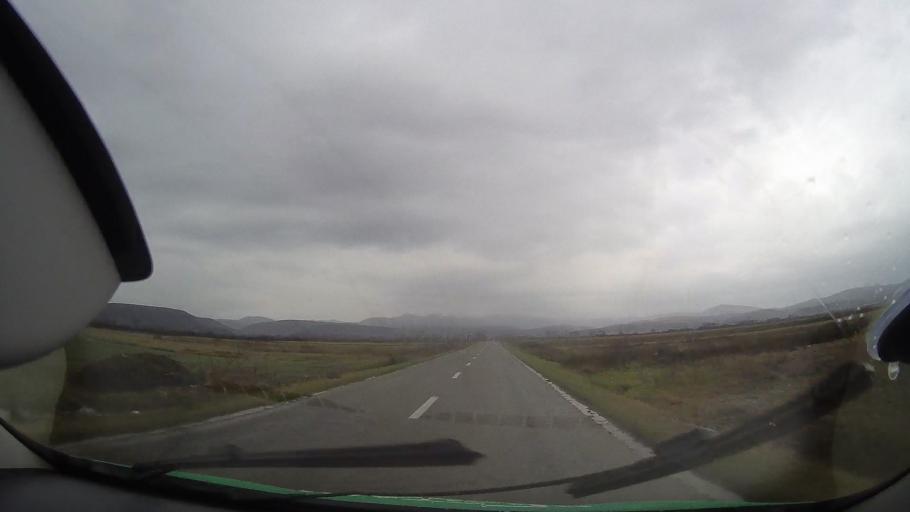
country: RO
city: Capalna
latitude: 46.7022
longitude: 22.0884
